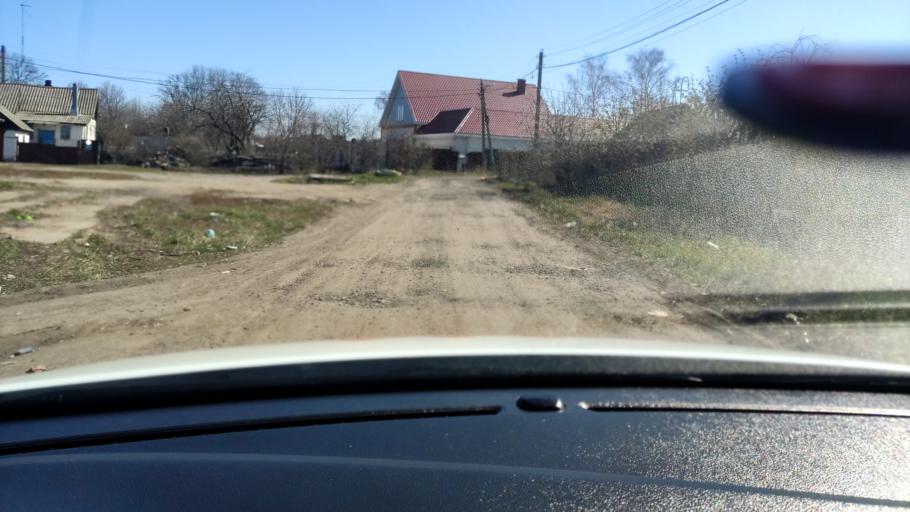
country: RU
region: Voronezj
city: Ramon'
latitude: 51.9840
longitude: 39.2231
